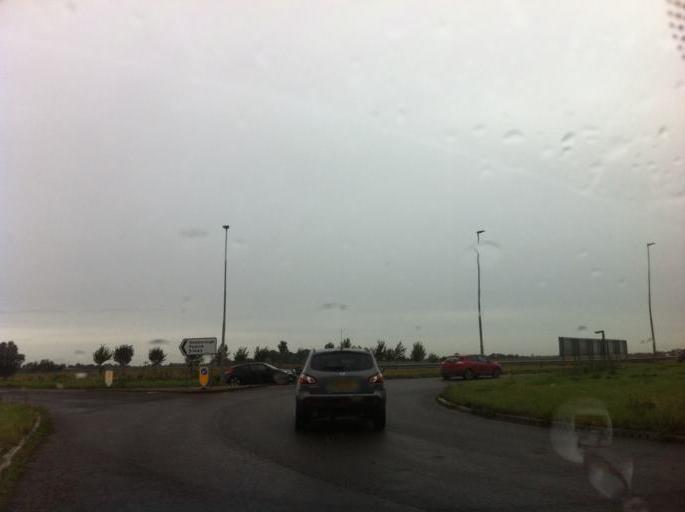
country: GB
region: England
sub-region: Peterborough
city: Newborough
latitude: 52.6371
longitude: -0.1957
